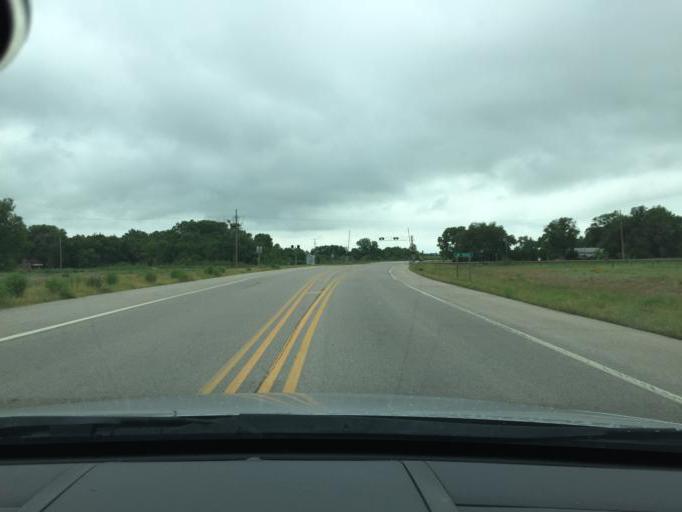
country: US
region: Kansas
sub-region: Reno County
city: Buhler
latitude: 38.1490
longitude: -97.8428
